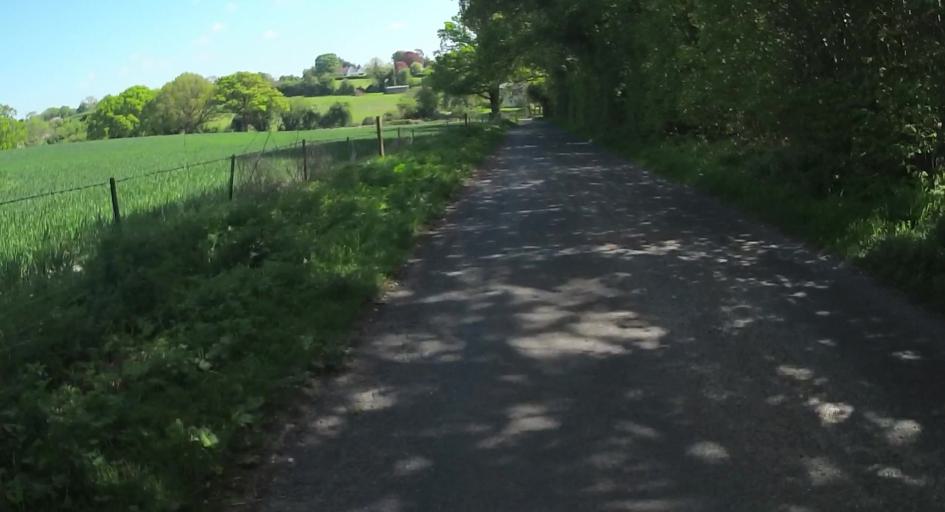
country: GB
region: England
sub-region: Hampshire
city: Four Marks
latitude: 51.1214
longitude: -1.0931
